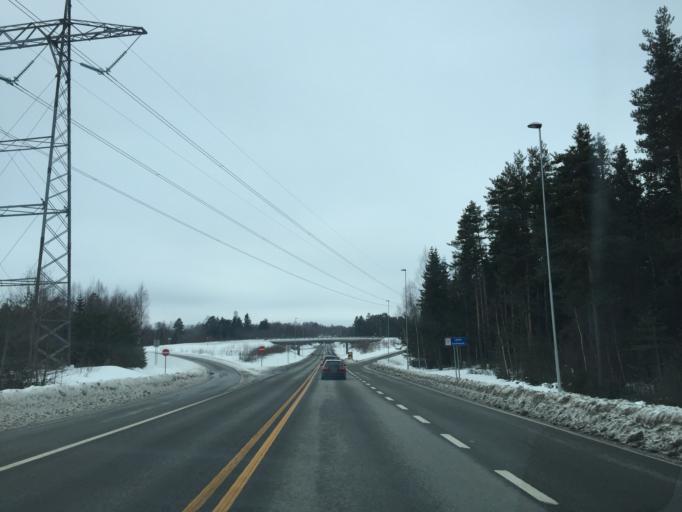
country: NO
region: Hedmark
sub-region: Loten
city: Loten
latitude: 60.7850
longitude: 11.3047
